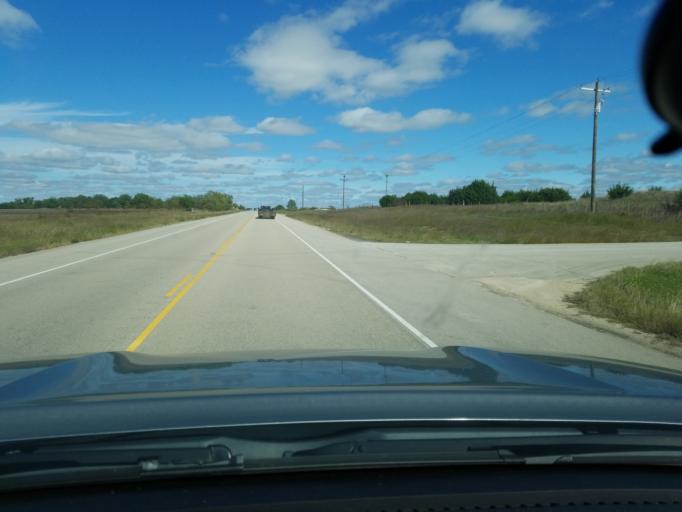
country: US
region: Texas
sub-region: Hamilton County
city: Hamilton
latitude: 31.6617
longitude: -98.1416
